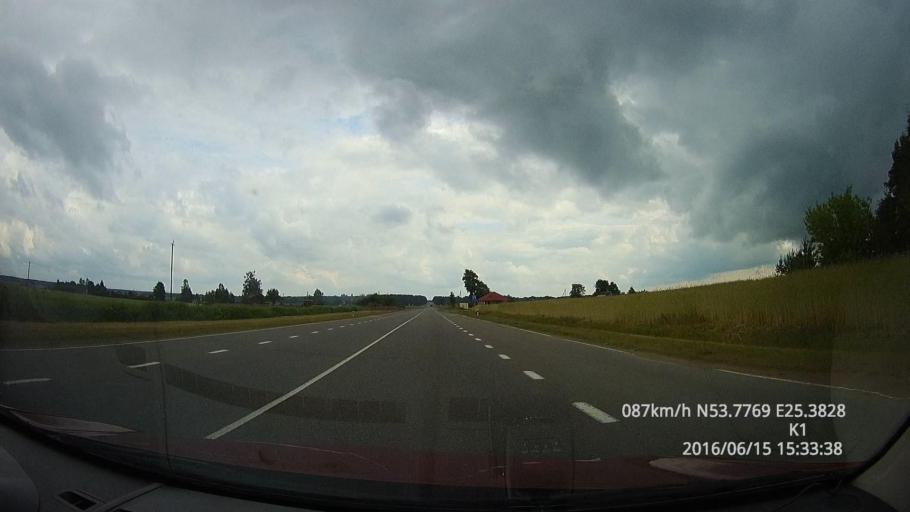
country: BY
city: Berezovka
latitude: 53.7761
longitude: 25.3832
